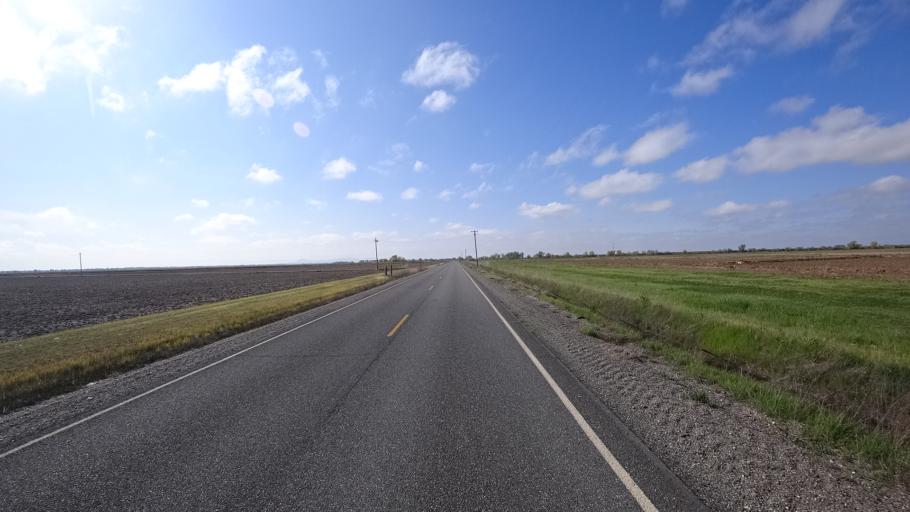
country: US
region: California
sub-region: Butte County
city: Durham
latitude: 39.4944
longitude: -121.9299
